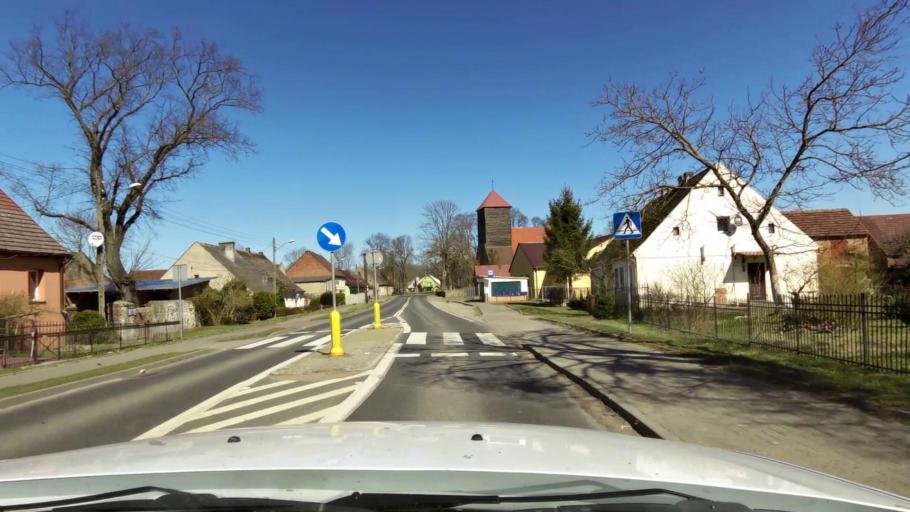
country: PL
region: West Pomeranian Voivodeship
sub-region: Powiat gryfinski
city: Cedynia
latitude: 52.8858
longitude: 14.2863
